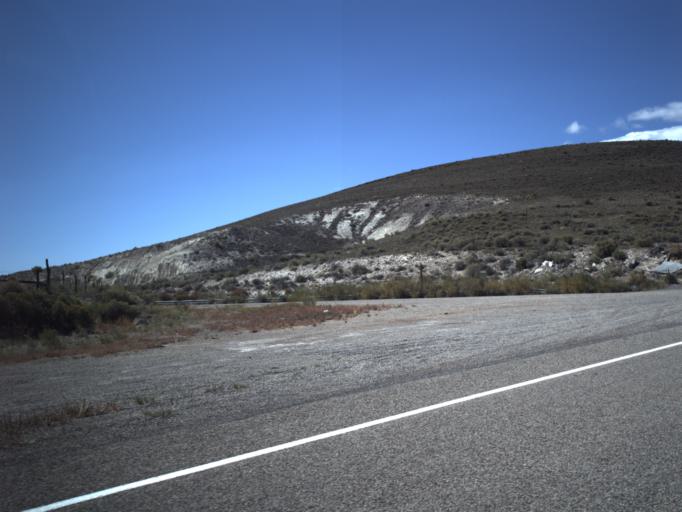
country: US
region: Utah
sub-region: Piute County
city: Junction
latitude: 38.2086
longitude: -112.2131
